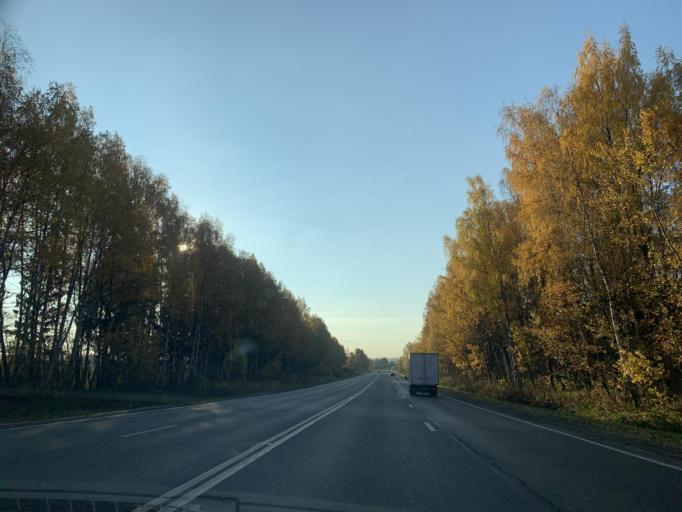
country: RU
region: Jaroslavl
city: Konstantinovskiy
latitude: 57.7730
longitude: 39.6664
